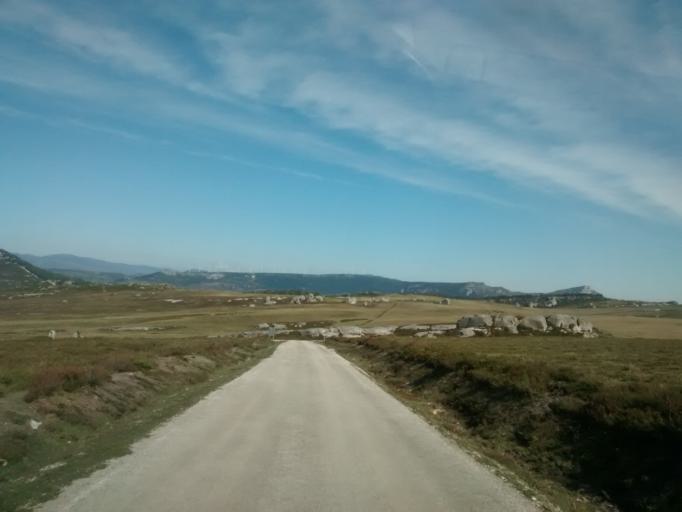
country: ES
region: Castille and Leon
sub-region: Provincia de Burgos
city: Arija
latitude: 42.9349
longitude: -3.9512
